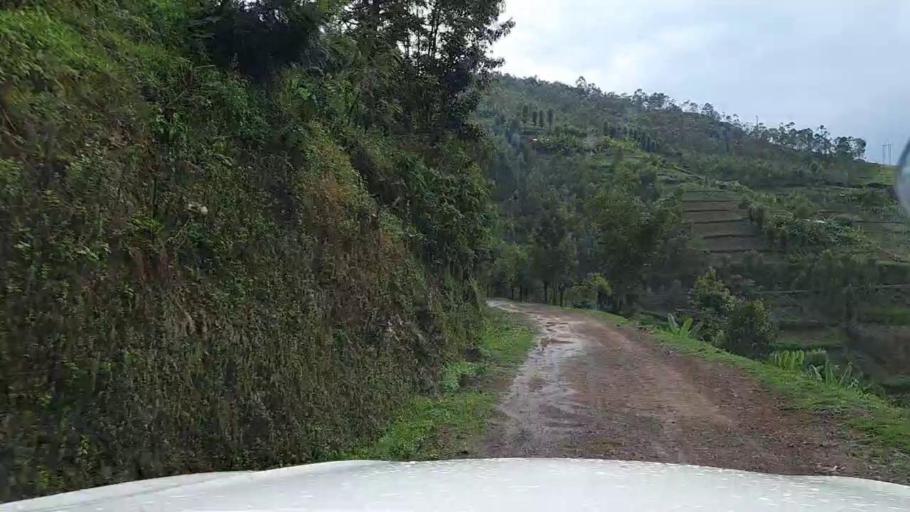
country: RW
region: Northern Province
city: Byumba
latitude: -1.7206
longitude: 29.9048
